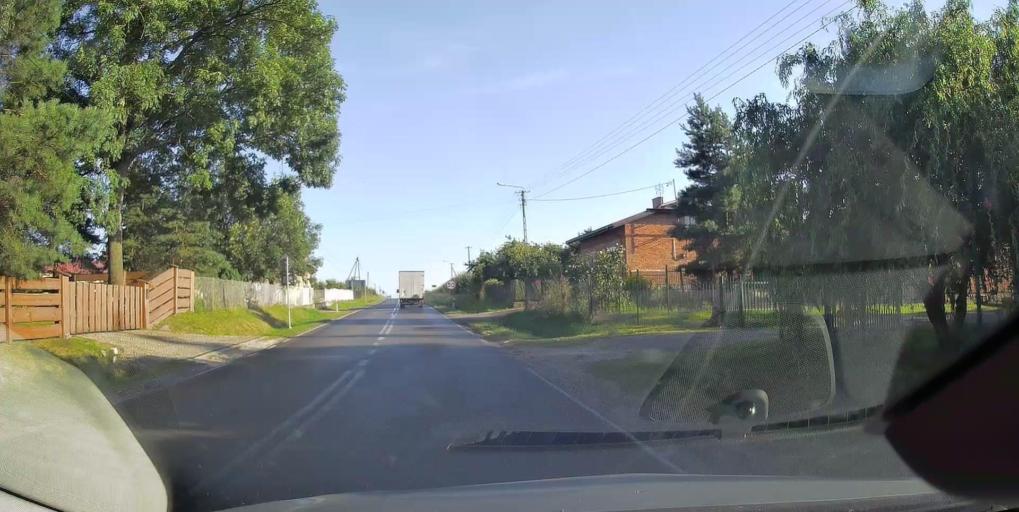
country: PL
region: Masovian Voivodeship
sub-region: Powiat grojecki
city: Bledow
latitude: 51.8092
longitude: 20.6998
